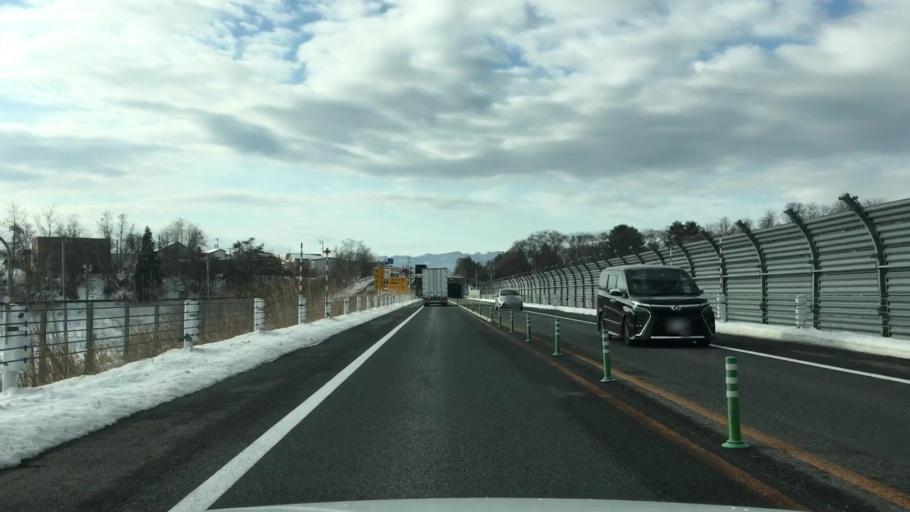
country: JP
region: Akita
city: Odate
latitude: 40.2789
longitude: 140.5371
